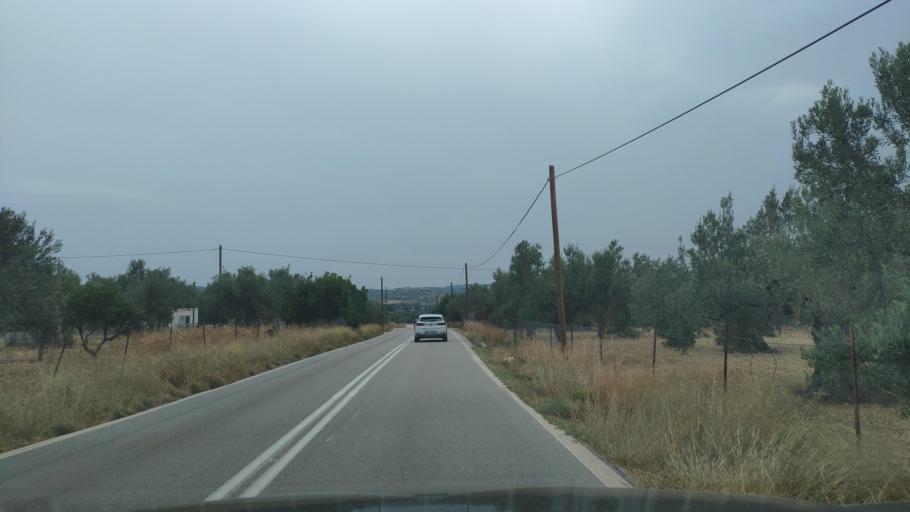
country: GR
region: Peloponnese
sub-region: Nomos Argolidos
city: Koilas
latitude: 37.4207
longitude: 23.1541
